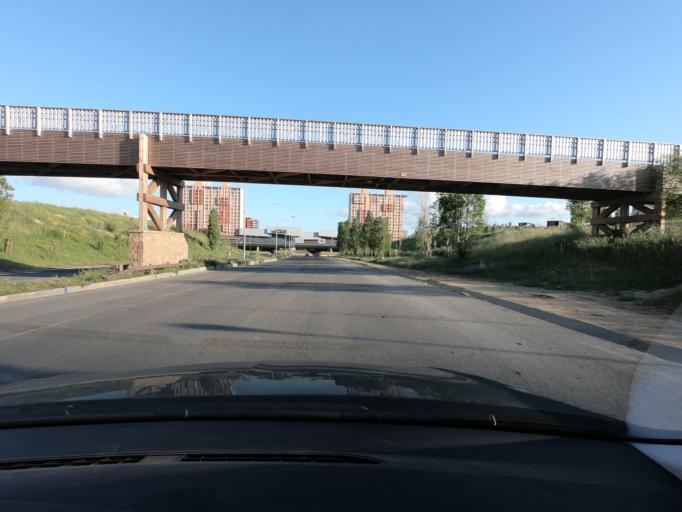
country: PT
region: Lisbon
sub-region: Loures
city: Moscavide
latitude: 38.7530
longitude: -9.1189
